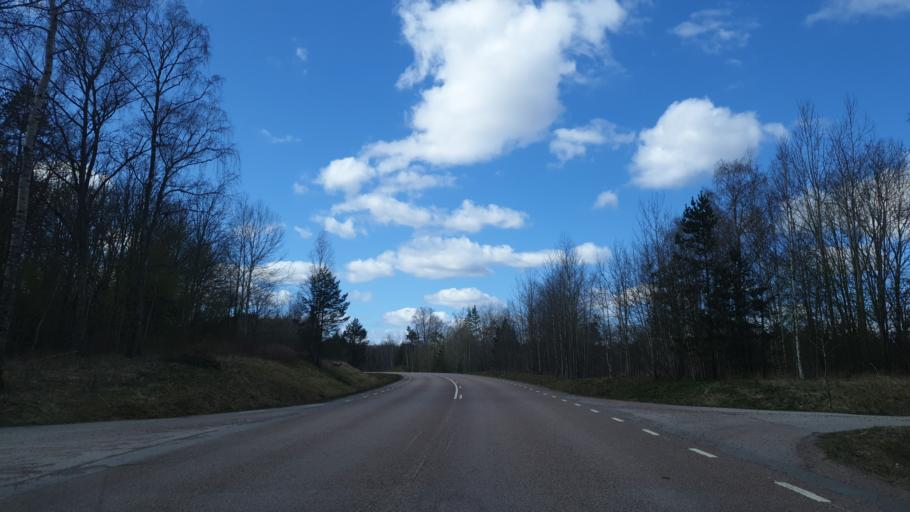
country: SE
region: Vaestmanland
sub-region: Kopings Kommun
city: Koping
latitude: 59.4986
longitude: 15.9799
